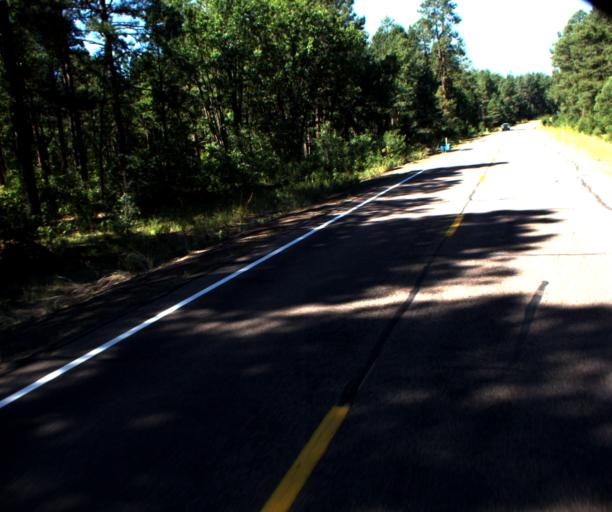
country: US
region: Arizona
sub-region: Navajo County
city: Pinetop-Lakeside
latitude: 34.0812
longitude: -109.8760
